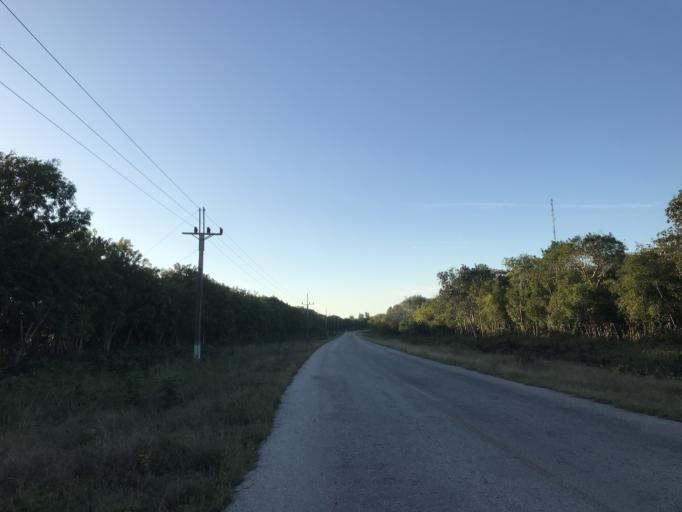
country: CU
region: Cienfuegos
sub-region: Municipio de Aguada de Pasajeros
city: Aguada de Pasajeros
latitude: 22.0679
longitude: -81.0486
